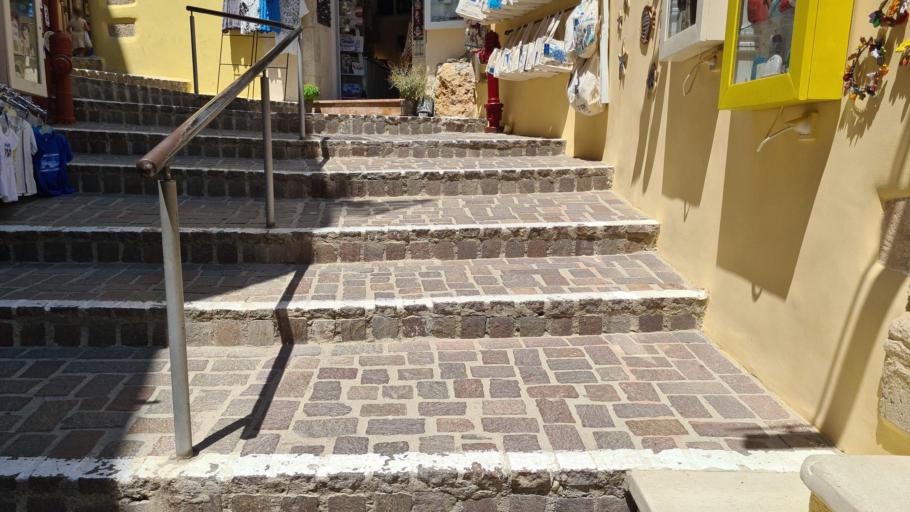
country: GR
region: Crete
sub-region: Nomos Chanias
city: Chania
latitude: 35.5167
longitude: 24.0160
